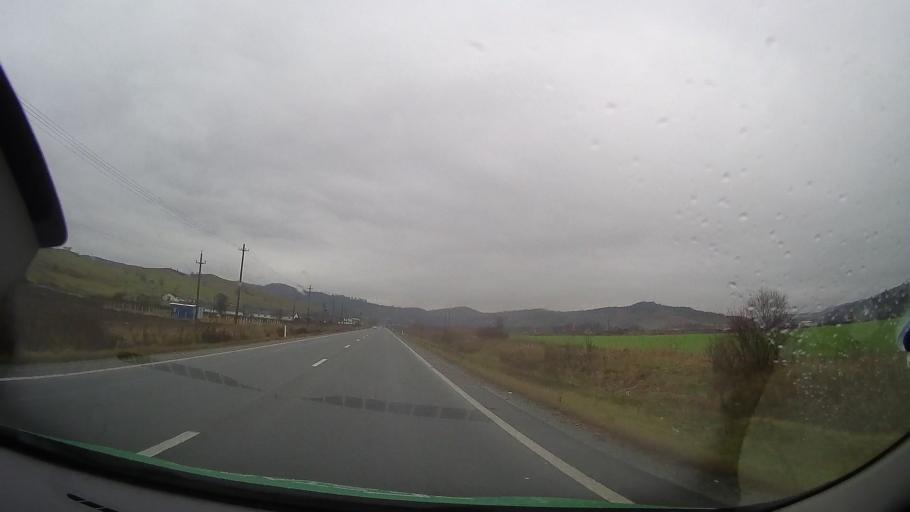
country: RO
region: Bistrita-Nasaud
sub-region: Comuna Teaca
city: Teaca
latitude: 46.9215
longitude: 24.4904
